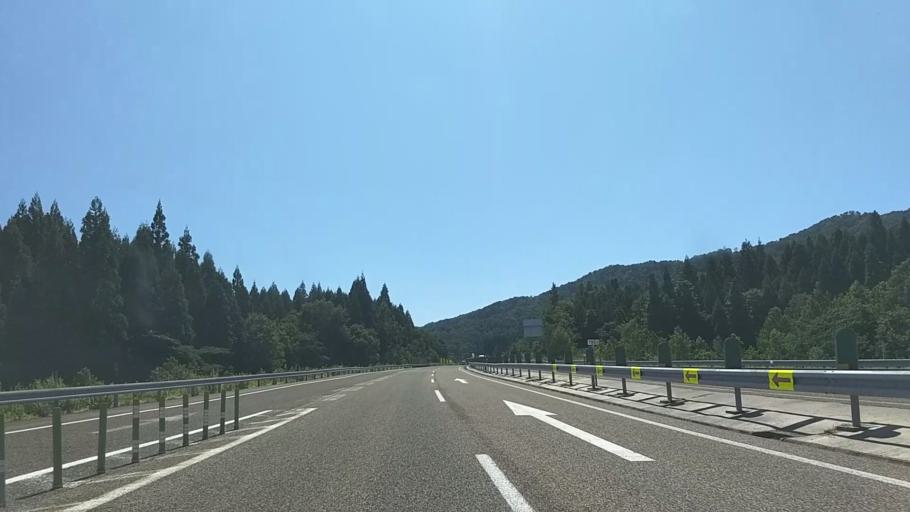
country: JP
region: Niigata
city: Joetsu
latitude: 37.0853
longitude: 138.2260
